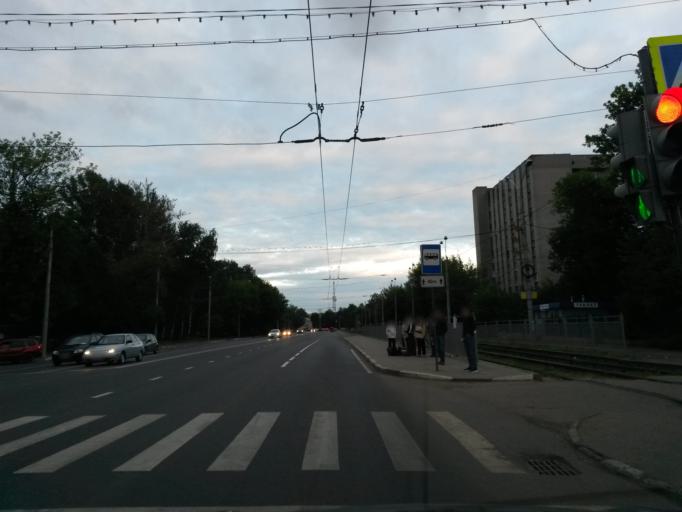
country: RU
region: Jaroslavl
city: Yaroslavl
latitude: 57.6403
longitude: 39.8566
